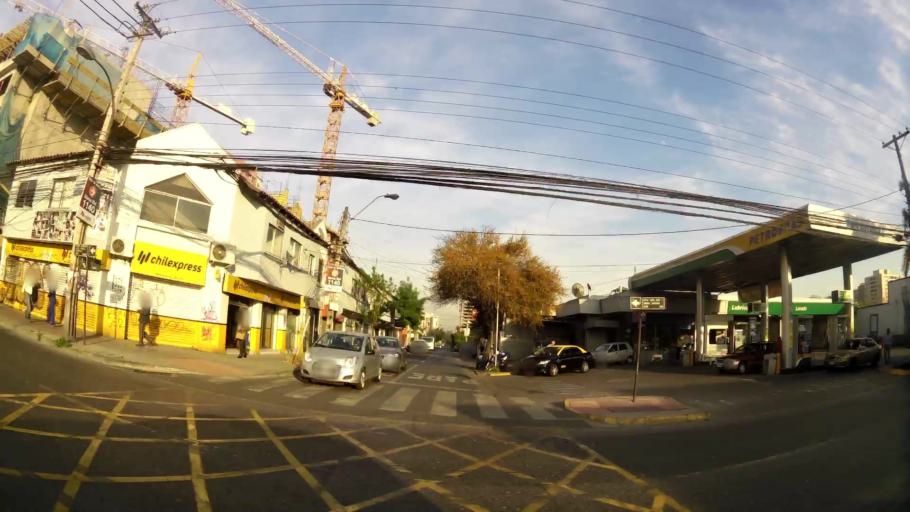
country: CL
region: Santiago Metropolitan
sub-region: Provincia de Santiago
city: Santiago
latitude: -33.4964
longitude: -70.6530
